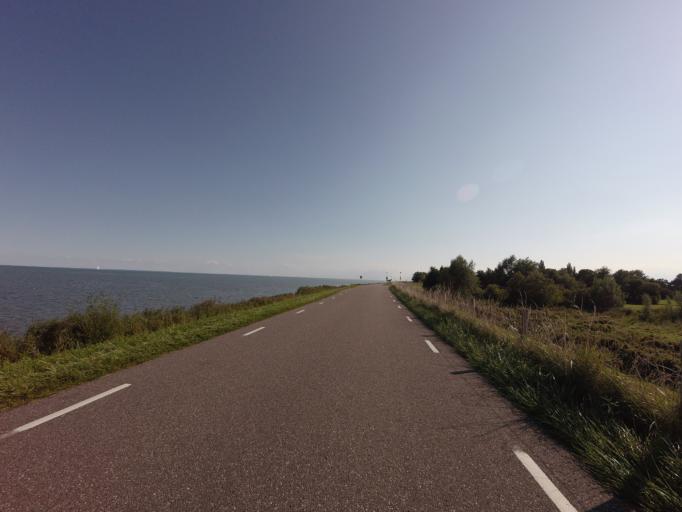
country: NL
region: North Holland
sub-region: Gemeente Enkhuizen
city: Enkhuizen
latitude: 52.6804
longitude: 5.2434
